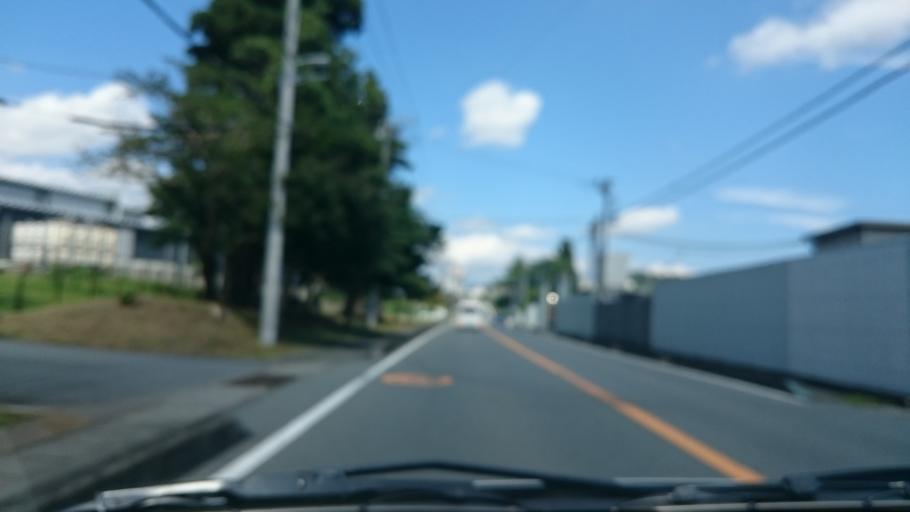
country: JP
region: Shizuoka
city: Gotemba
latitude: 35.2807
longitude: 138.9270
